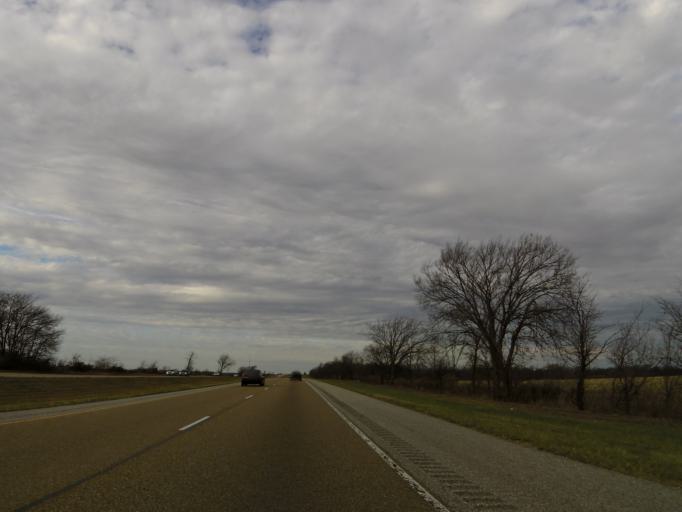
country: US
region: Illinois
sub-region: Clinton County
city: Wamac
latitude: 38.3899
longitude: -89.2273
